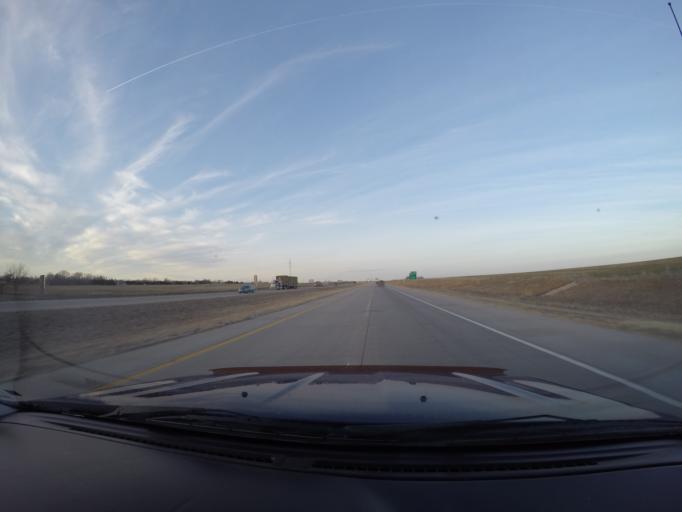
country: US
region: Kansas
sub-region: Saline County
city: Salina
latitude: 38.8630
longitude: -97.6454
